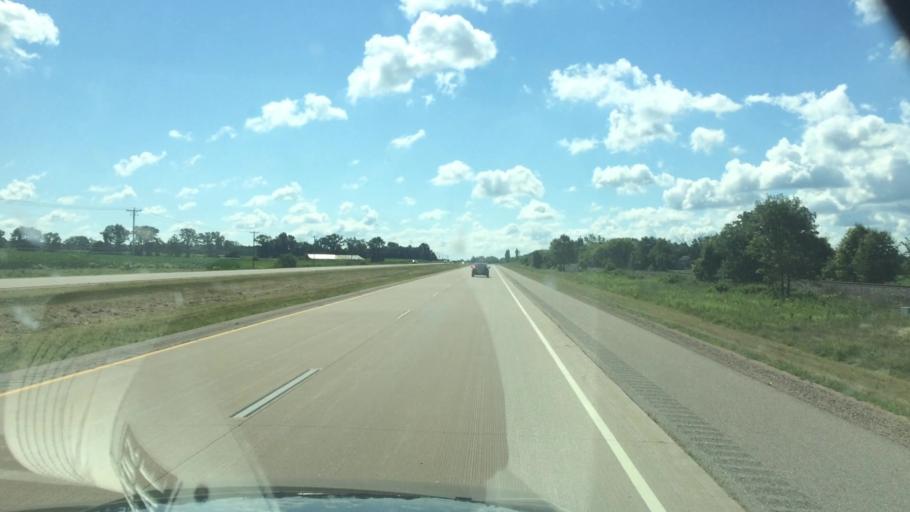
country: US
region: Wisconsin
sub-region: Portage County
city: Amherst
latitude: 44.4834
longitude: -89.3454
